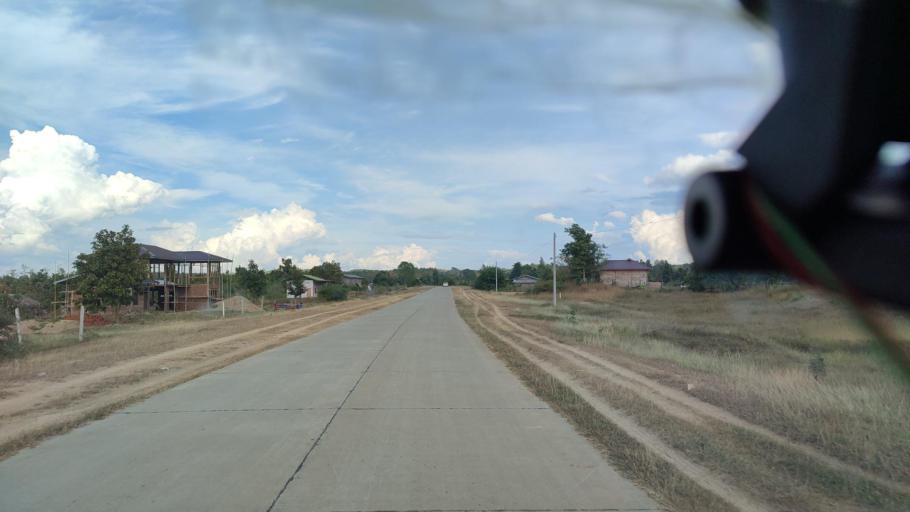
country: MM
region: Mandalay
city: Yamethin
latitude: 20.0956
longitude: 96.0235
